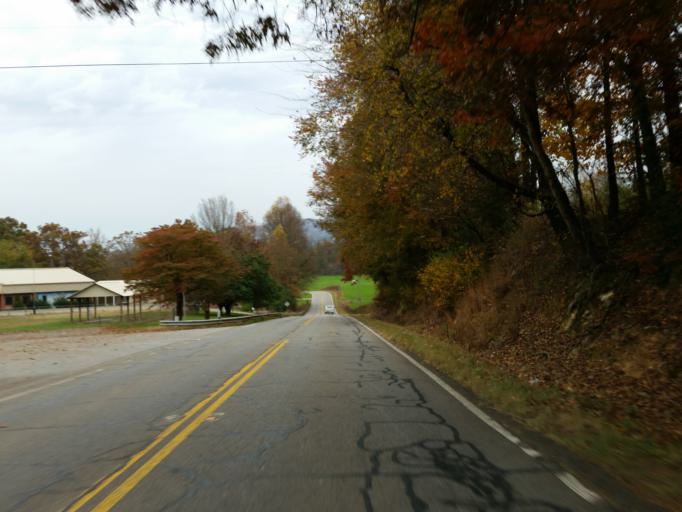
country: US
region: Georgia
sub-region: Gilmer County
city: Ellijay
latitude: 34.6339
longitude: -84.3874
